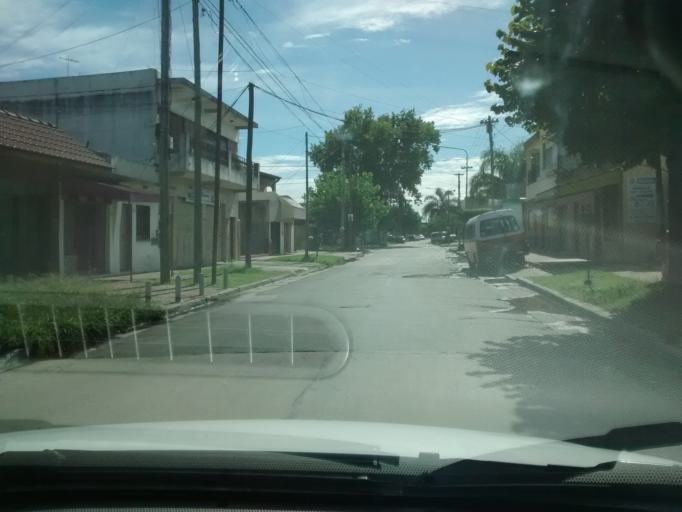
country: AR
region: Buenos Aires
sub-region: Partido de Moron
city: Moron
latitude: -34.6662
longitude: -58.6090
